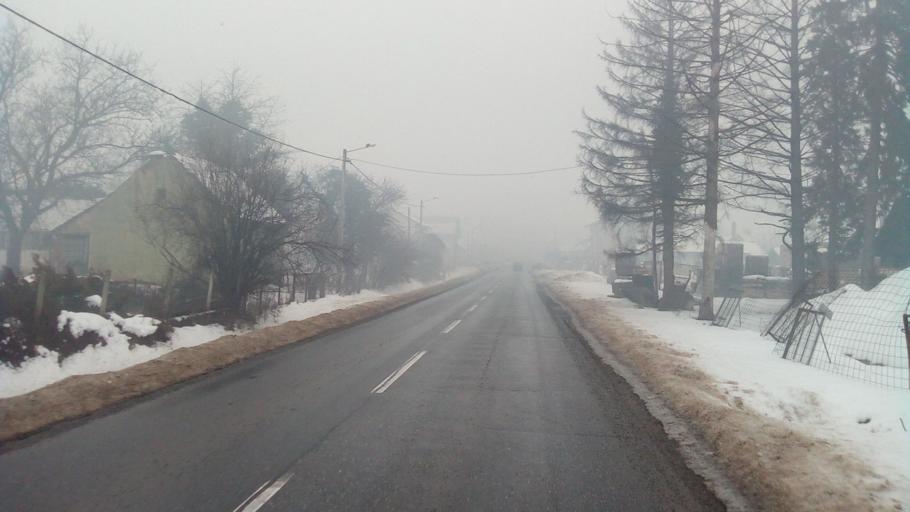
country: HR
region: Sisacko-Moslavacka
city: Petrinja
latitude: 45.4243
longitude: 16.2850
